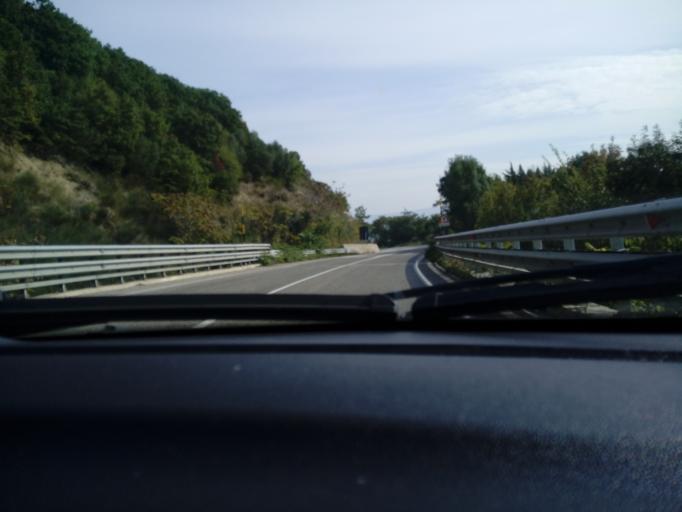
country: IT
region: Molise
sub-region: Provincia di Campobasso
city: Riccia
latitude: 41.5127
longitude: 14.8436
